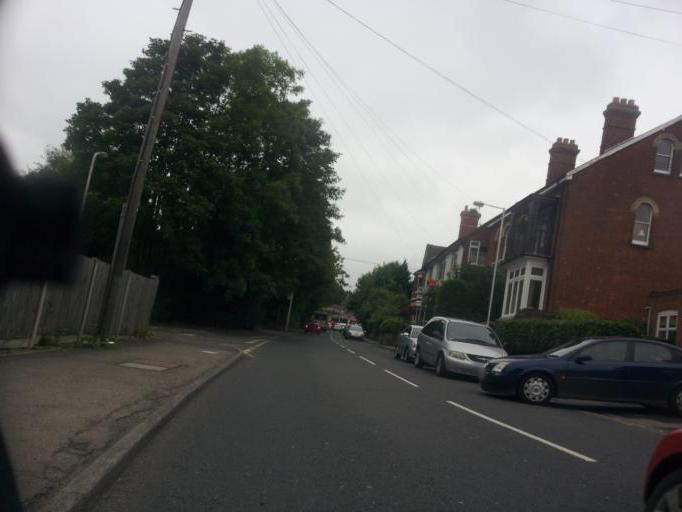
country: GB
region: England
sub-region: Kent
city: Wateringbury
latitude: 51.2532
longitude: 0.4214
